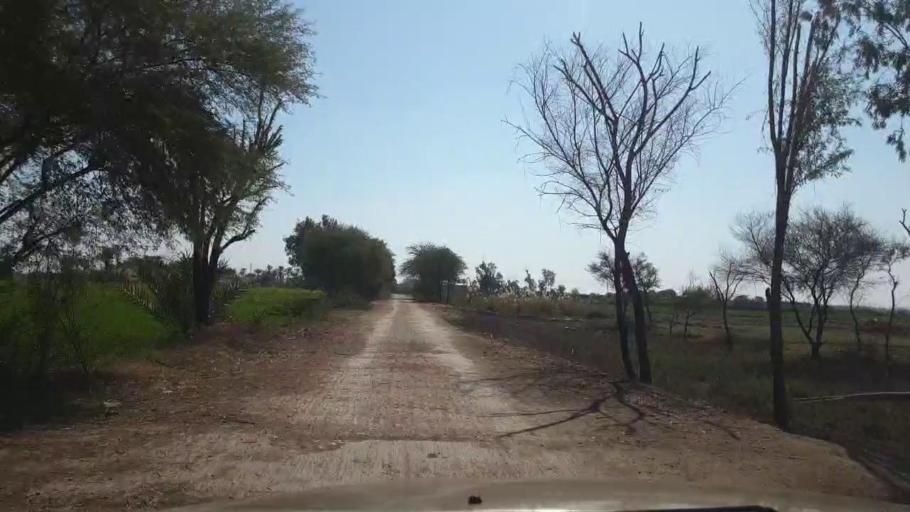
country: PK
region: Sindh
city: Mirpur Khas
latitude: 25.5565
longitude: 69.0665
